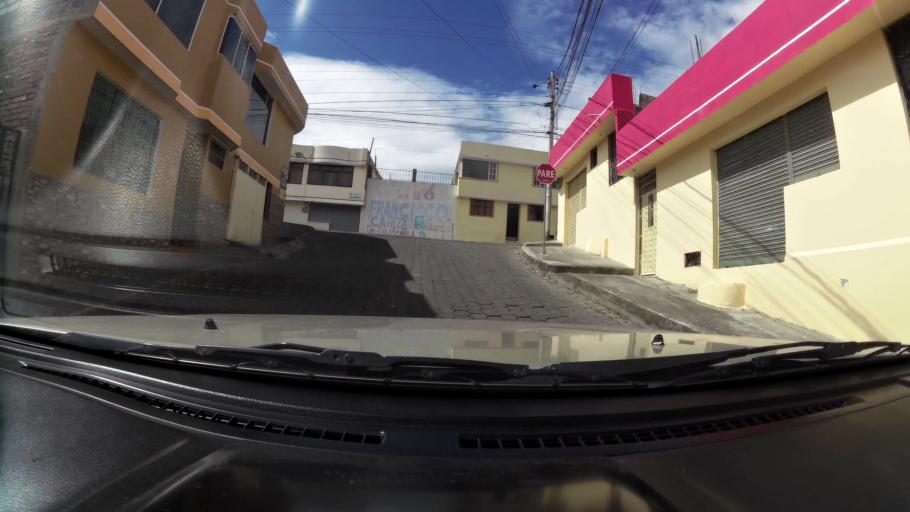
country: EC
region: Cotopaxi
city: Latacunga
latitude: -0.9314
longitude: -78.6006
